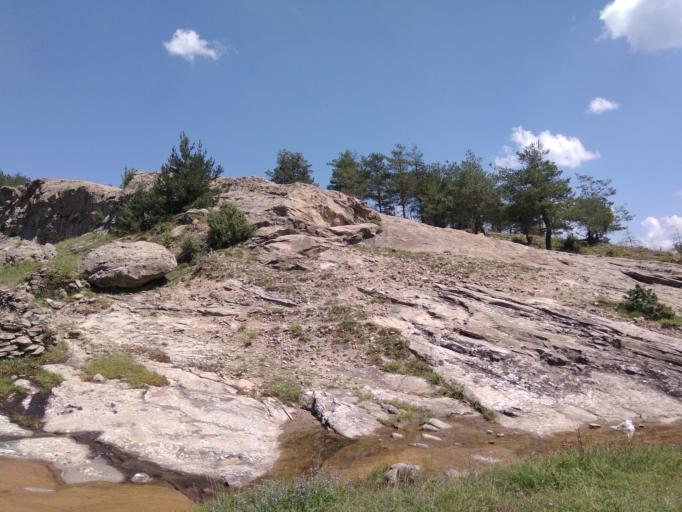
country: BG
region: Smolyan
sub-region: Obshtina Zlatograd
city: Zlatograd
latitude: 41.3627
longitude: 25.1953
